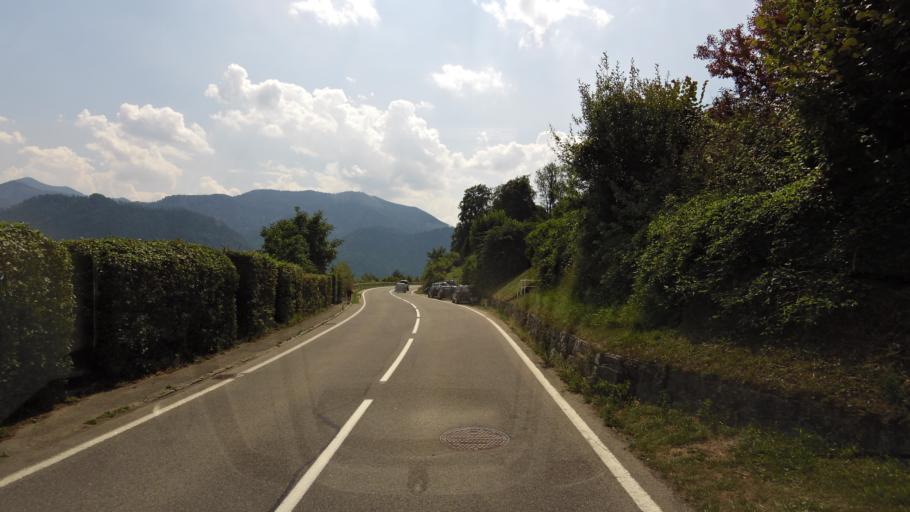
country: AT
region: Upper Austria
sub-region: Politischer Bezirk Vocklabruck
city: Steinbach am Attersee
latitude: 47.8173
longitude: 13.5076
